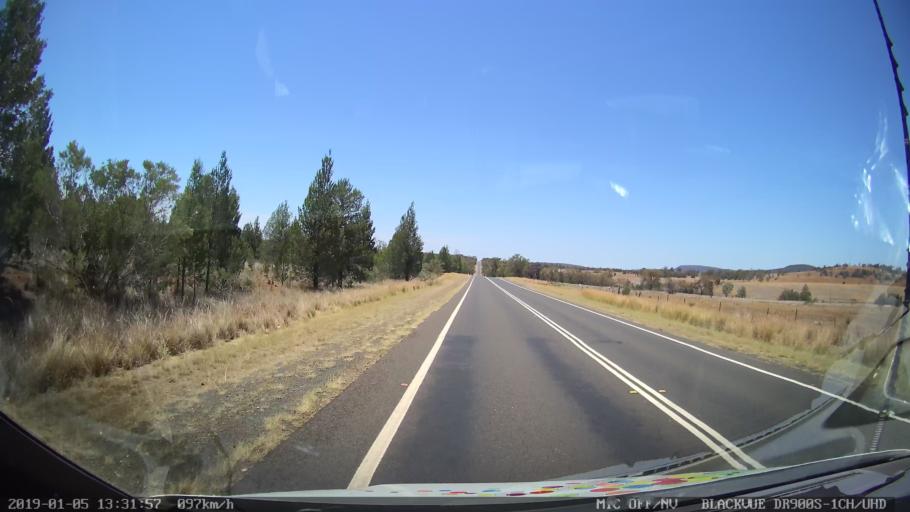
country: AU
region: New South Wales
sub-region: Gunnedah
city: Gunnedah
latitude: -31.0079
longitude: 150.0921
